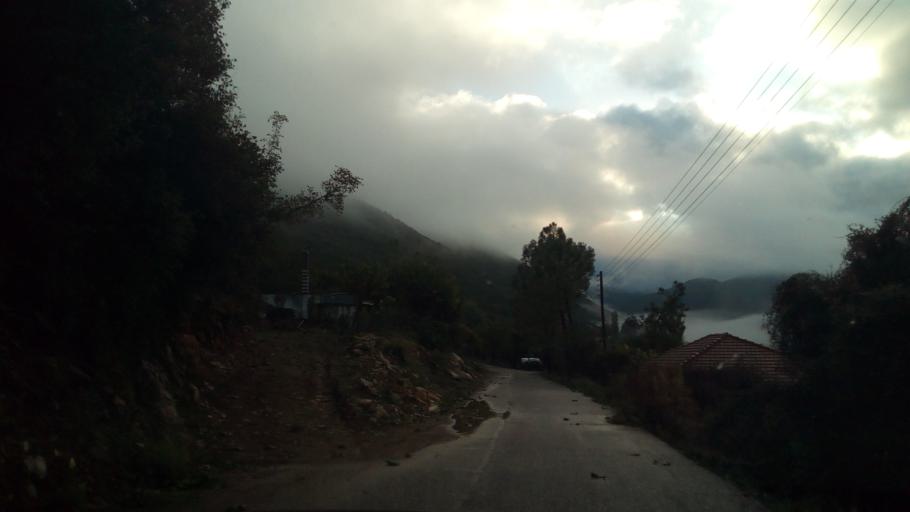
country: GR
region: West Greece
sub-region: Nomos Aitolias kai Akarnanias
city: Thermo
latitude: 38.5195
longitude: 21.7712
